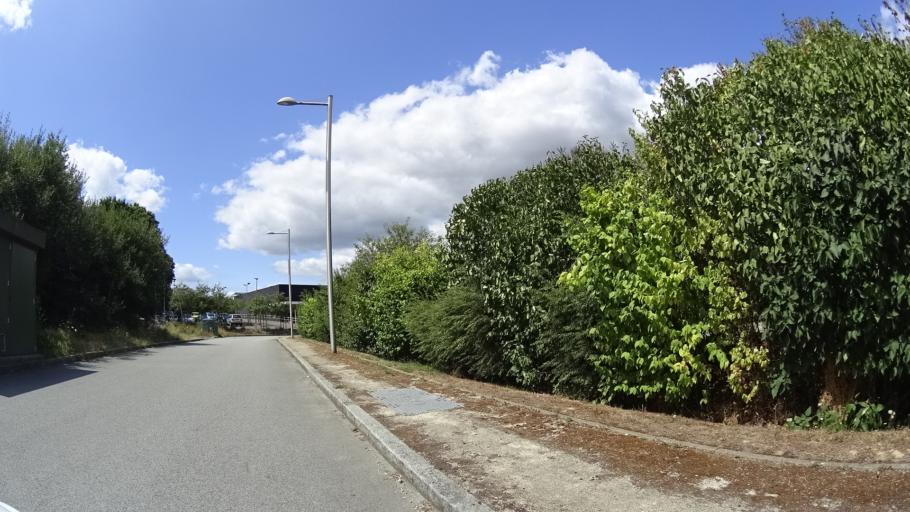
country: FR
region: Brittany
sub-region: Departement d'Ille-et-Vilaine
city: La Chapelle-des-Fougeretz
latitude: 48.2041
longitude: -1.7278
